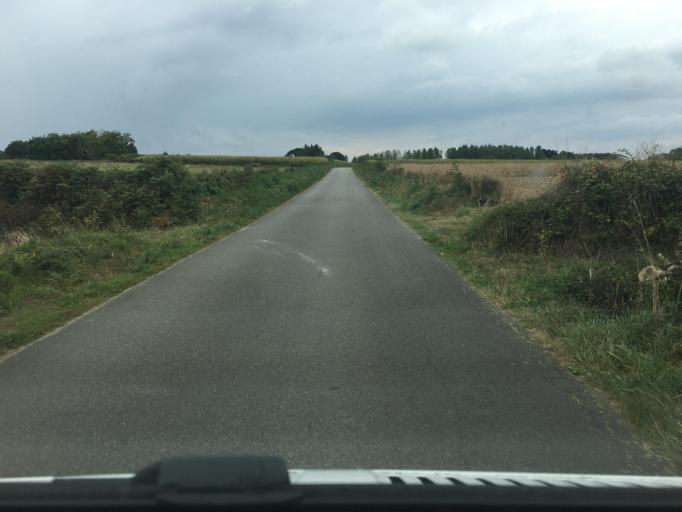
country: FR
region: Brittany
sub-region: Departement du Finistere
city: Beuzec-Cap-Sizun
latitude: 48.0751
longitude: -4.4755
